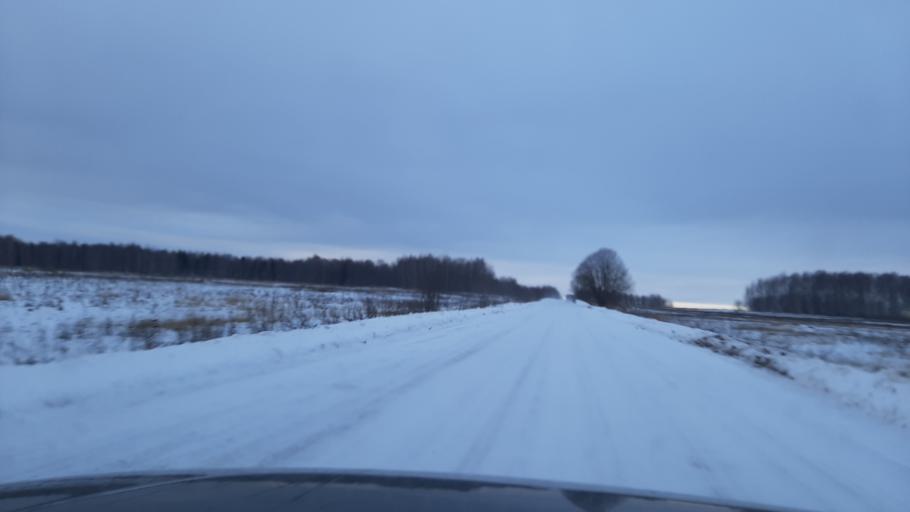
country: RU
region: Kostroma
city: Volgorechensk
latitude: 57.4495
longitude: 41.0240
